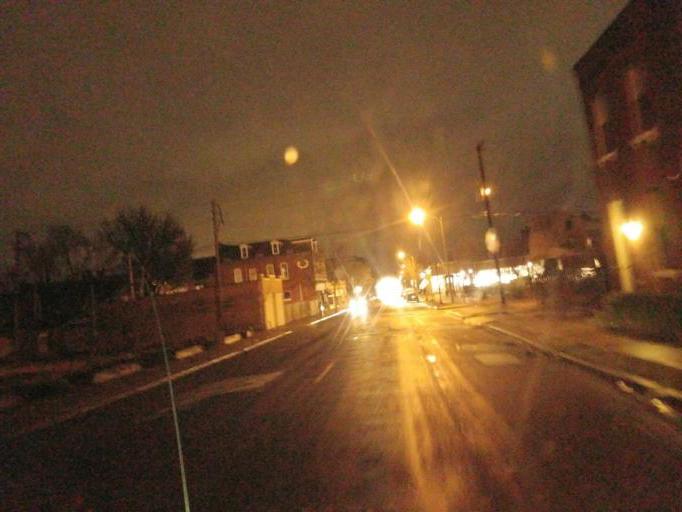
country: US
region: Missouri
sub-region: City of Saint Louis
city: St. Louis
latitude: 38.6510
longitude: -90.1988
